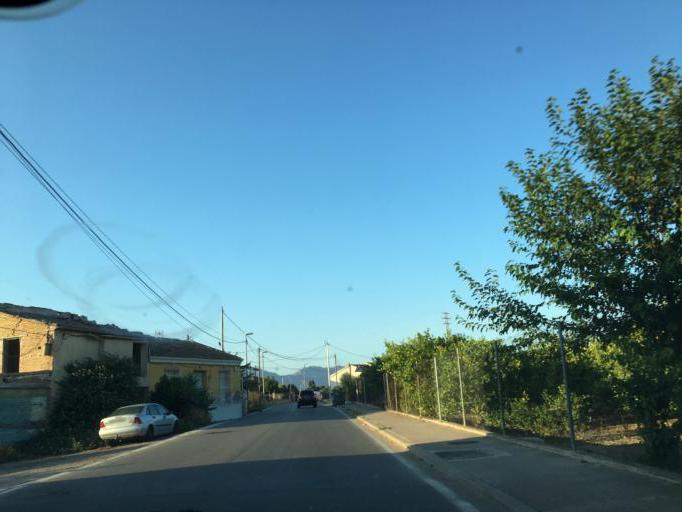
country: ES
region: Murcia
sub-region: Murcia
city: Murcia
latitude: 38.0072
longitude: -1.0772
